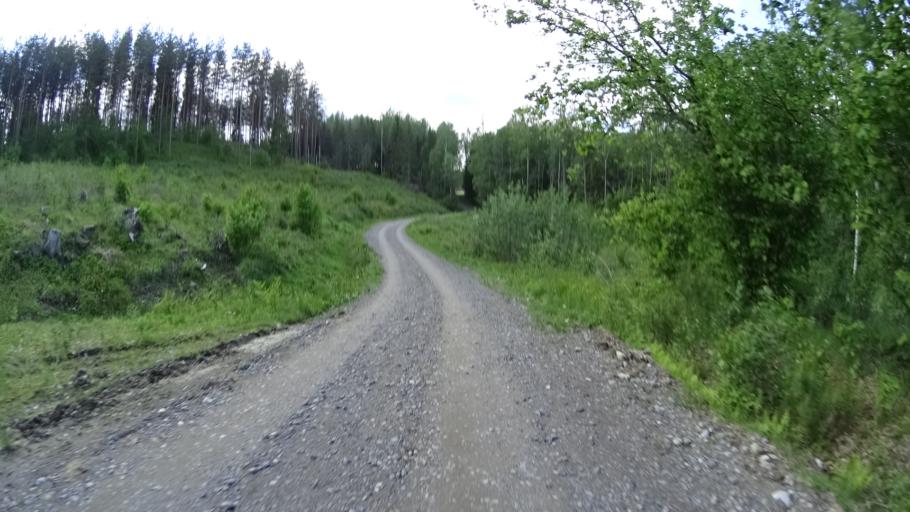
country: FI
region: Uusimaa
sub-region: Raaseporin
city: Karis
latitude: 60.1561
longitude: 23.6183
